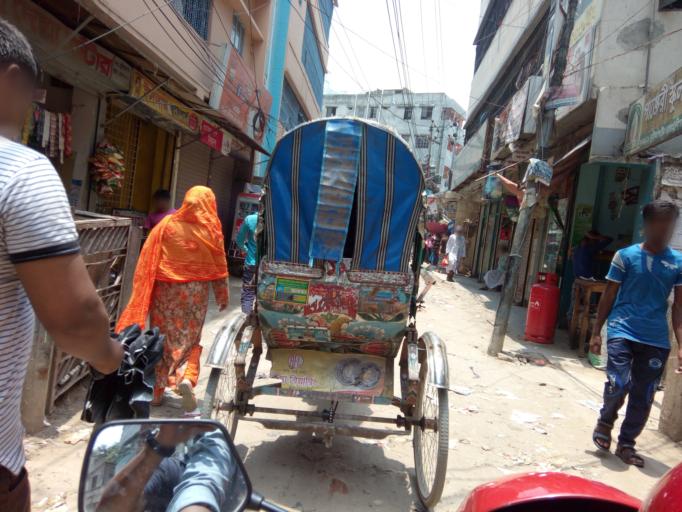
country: BD
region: Dhaka
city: Paltan
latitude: 23.7533
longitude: 90.4325
